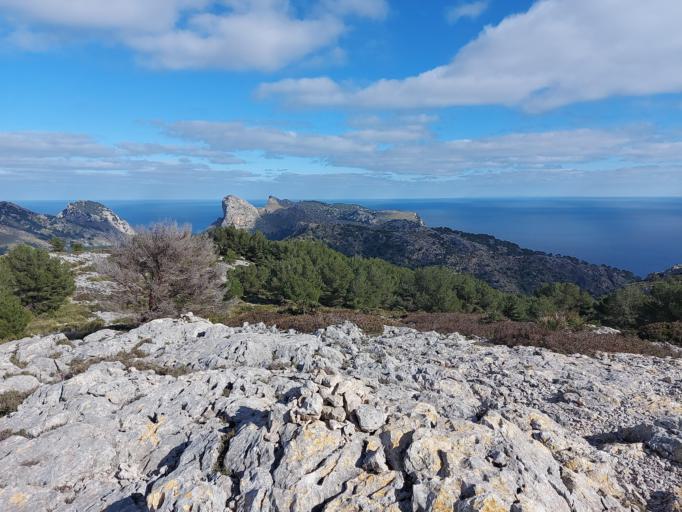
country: ES
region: Balearic Islands
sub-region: Illes Balears
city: Alcudia
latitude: 39.9321
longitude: 3.1491
